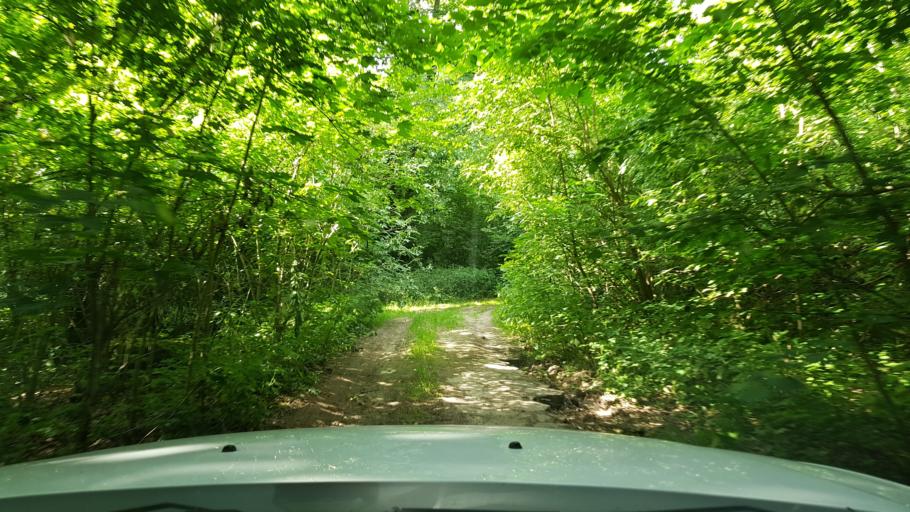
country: PL
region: West Pomeranian Voivodeship
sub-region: Powiat gryfinski
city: Moryn
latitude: 52.9215
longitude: 14.3617
